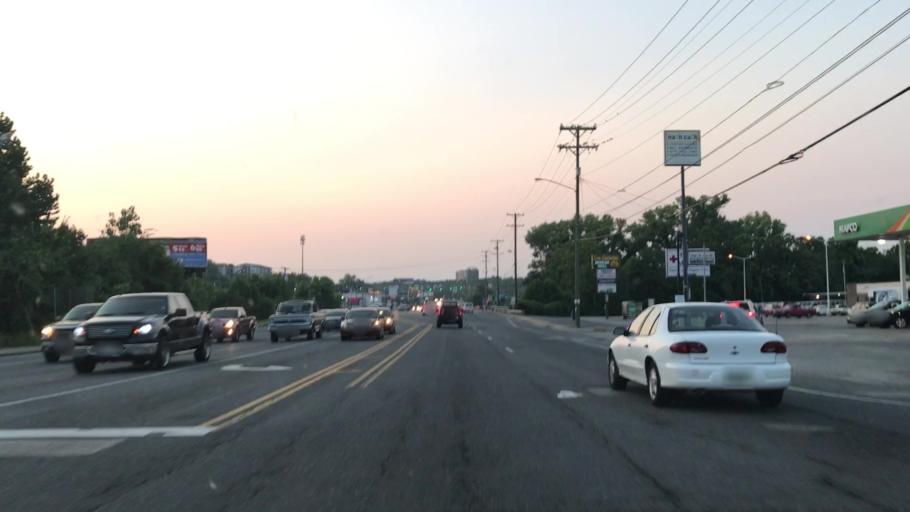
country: US
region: Tennessee
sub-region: Davidson County
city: Oak Hill
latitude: 36.0772
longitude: -86.7255
